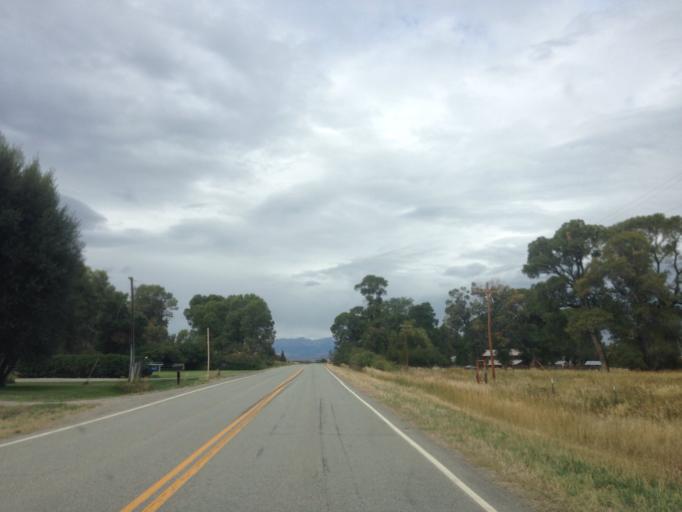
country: US
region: Montana
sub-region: Sweet Grass County
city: Big Timber
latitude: 45.7748
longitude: -109.8039
